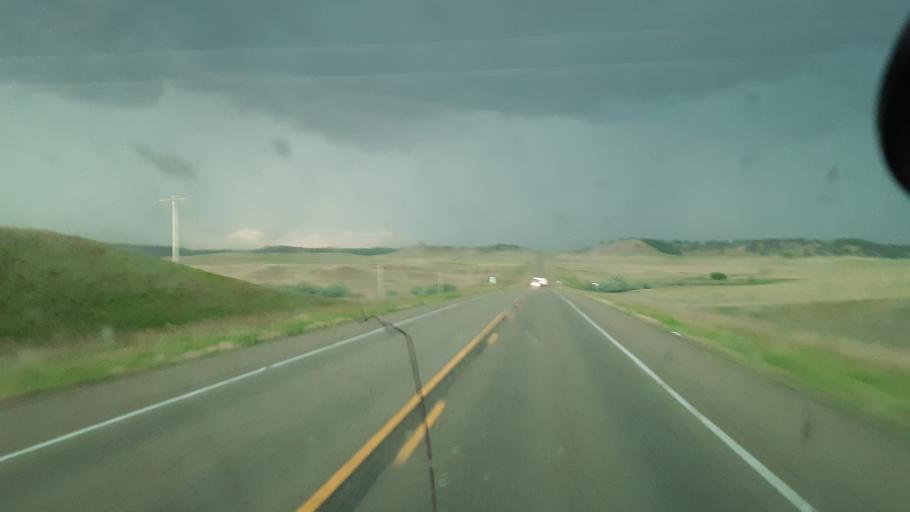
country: US
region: Montana
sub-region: Powder River County
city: Broadus
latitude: 45.4677
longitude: -105.4706
